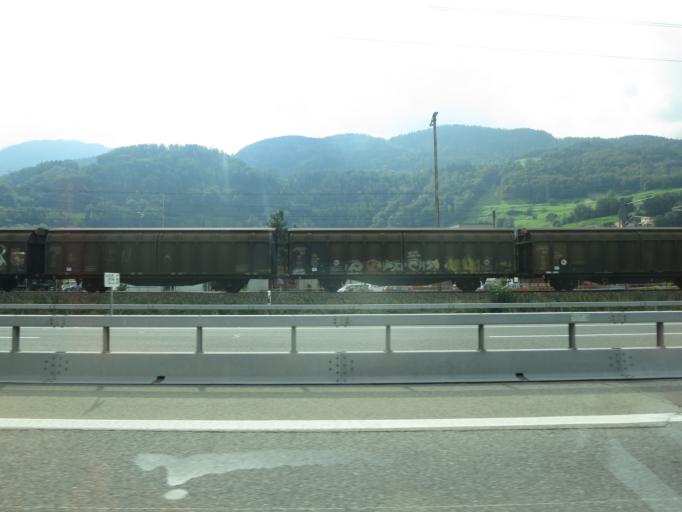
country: CH
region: Saint Gallen
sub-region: Wahlkreis Sarganserland
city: Sargans
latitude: 47.0598
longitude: 9.4054
